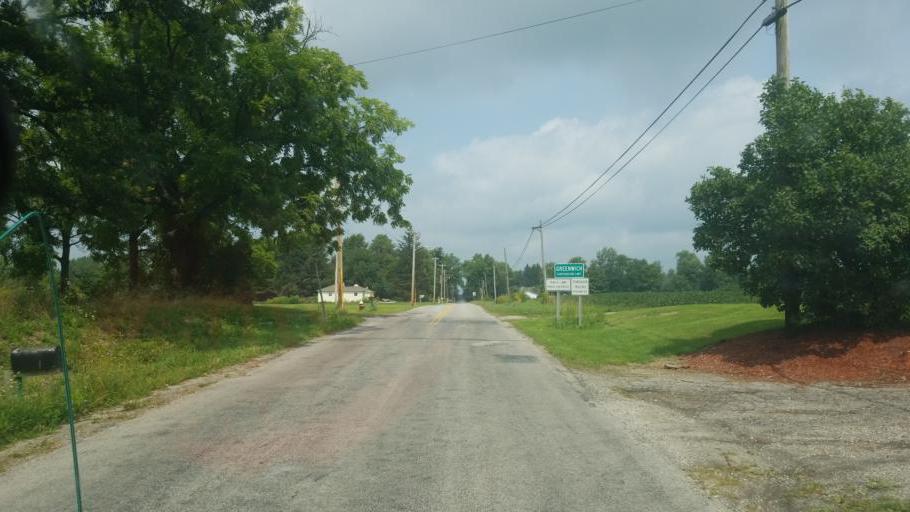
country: US
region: Ohio
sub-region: Huron County
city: Greenwich
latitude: 41.0198
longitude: -82.5103
